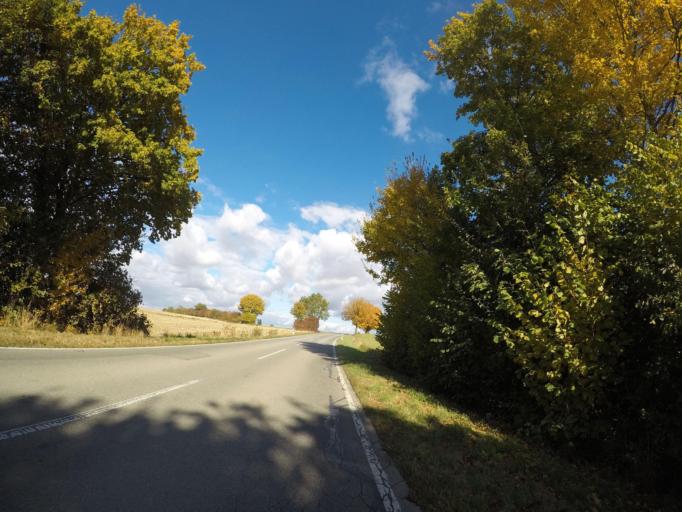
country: DE
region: Baden-Wuerttemberg
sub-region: Tuebingen Region
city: Grundsheim
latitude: 48.1589
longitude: 9.6742
